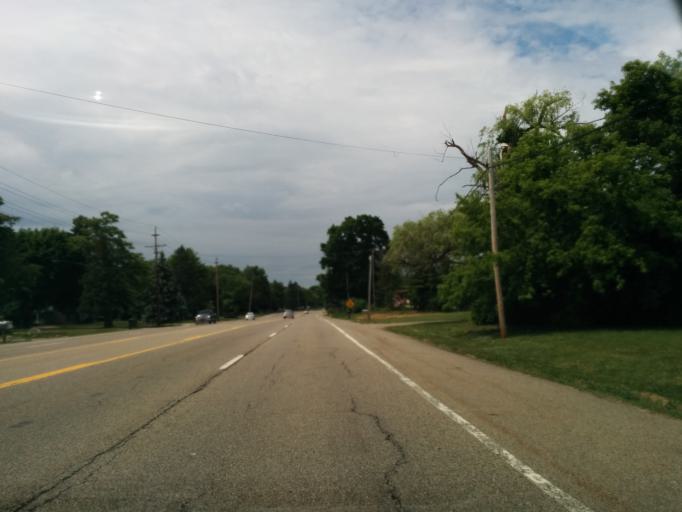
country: US
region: Michigan
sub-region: Oakland County
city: Wolverine Lake
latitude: 42.5527
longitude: -83.4534
